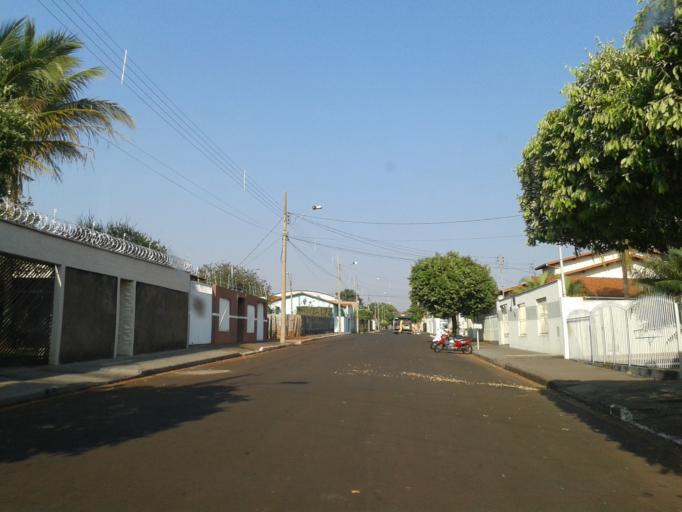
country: BR
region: Minas Gerais
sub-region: Ituiutaba
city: Ituiutaba
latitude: -18.9763
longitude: -49.4752
